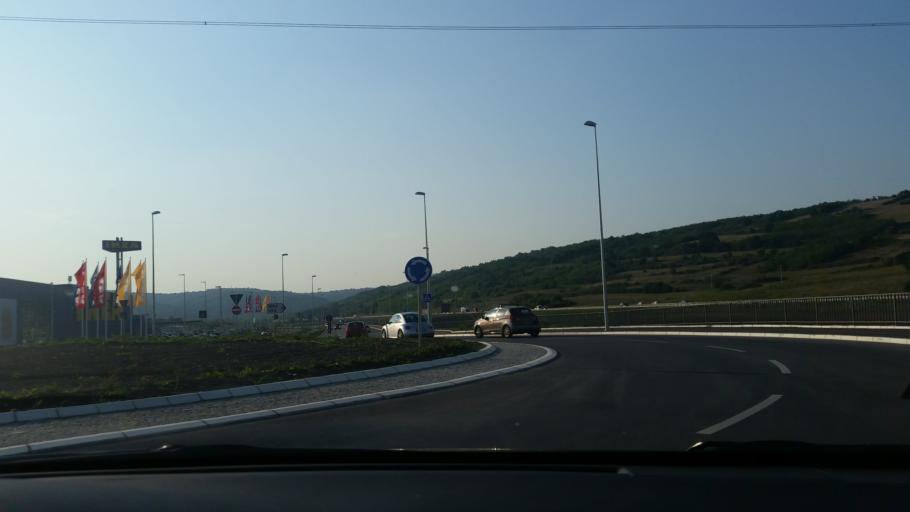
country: RS
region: Central Serbia
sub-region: Belgrade
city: Zvezdara
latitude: 44.7099
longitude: 20.5657
